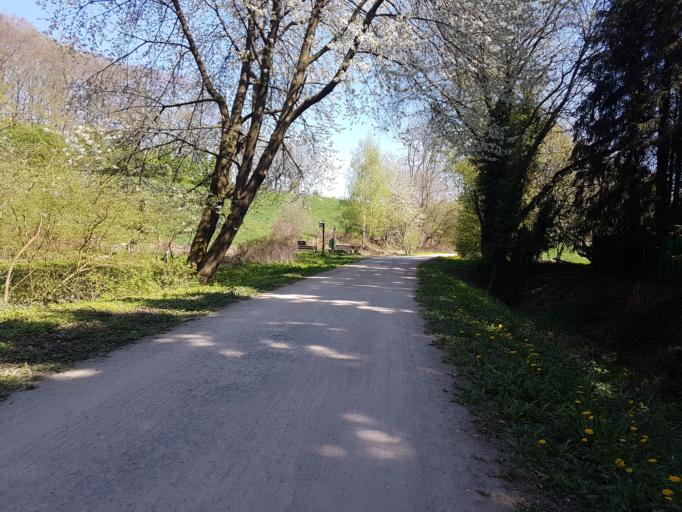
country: DE
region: North Rhine-Westphalia
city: Sprockhovel
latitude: 51.3303
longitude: 7.2580
